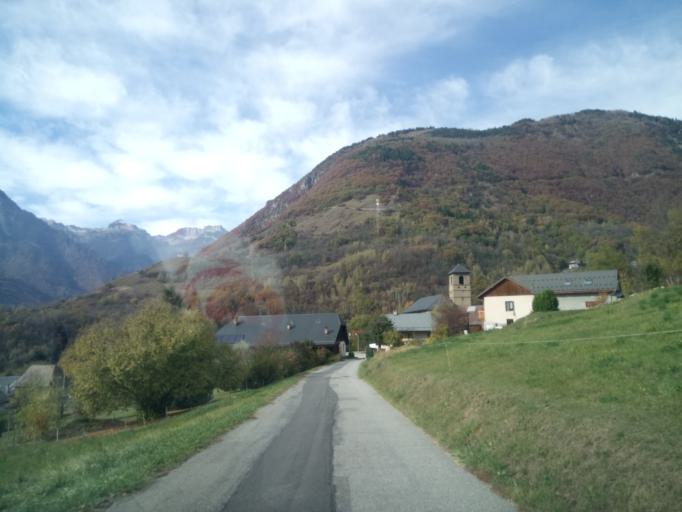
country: FR
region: Rhone-Alpes
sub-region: Departement de la Savoie
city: La Chambre
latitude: 45.3664
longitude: 6.3153
